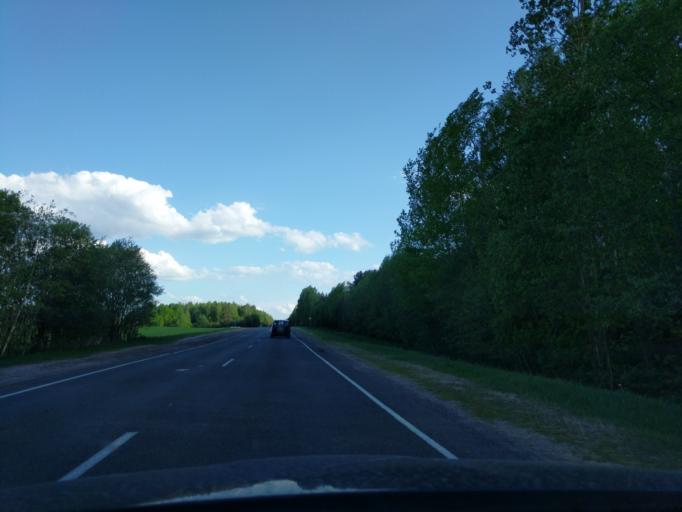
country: BY
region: Minsk
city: Kryvichy
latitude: 54.6080
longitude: 27.1806
